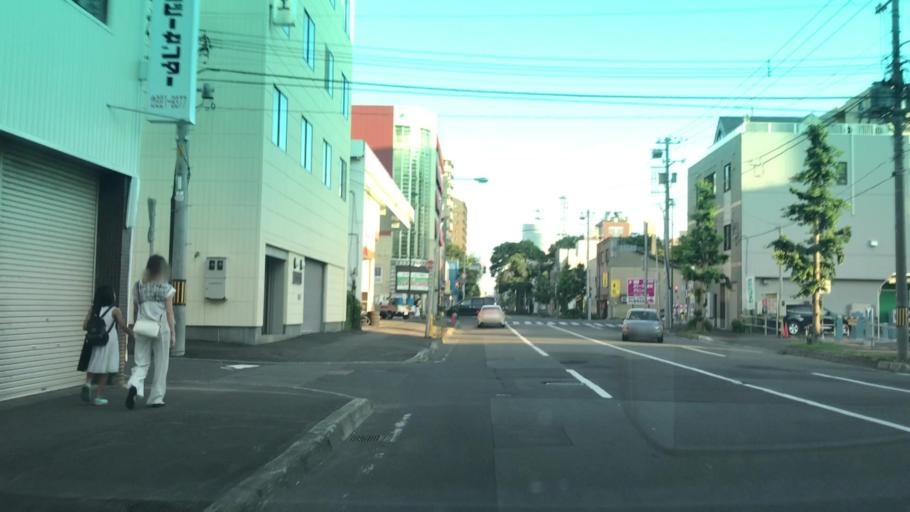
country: JP
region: Hokkaido
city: Sapporo
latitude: 43.0654
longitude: 141.3347
